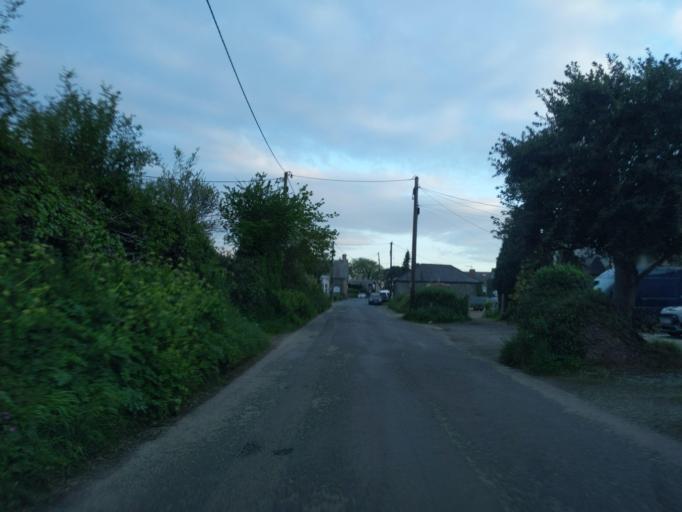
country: GB
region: England
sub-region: Cornwall
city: Polzeath
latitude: 50.5599
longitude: -4.8728
